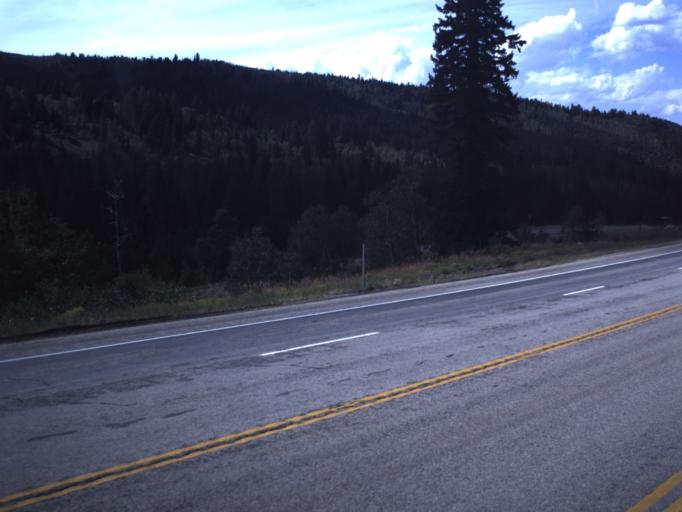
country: US
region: Utah
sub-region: Wasatch County
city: Heber
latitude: 40.3123
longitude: -111.2568
